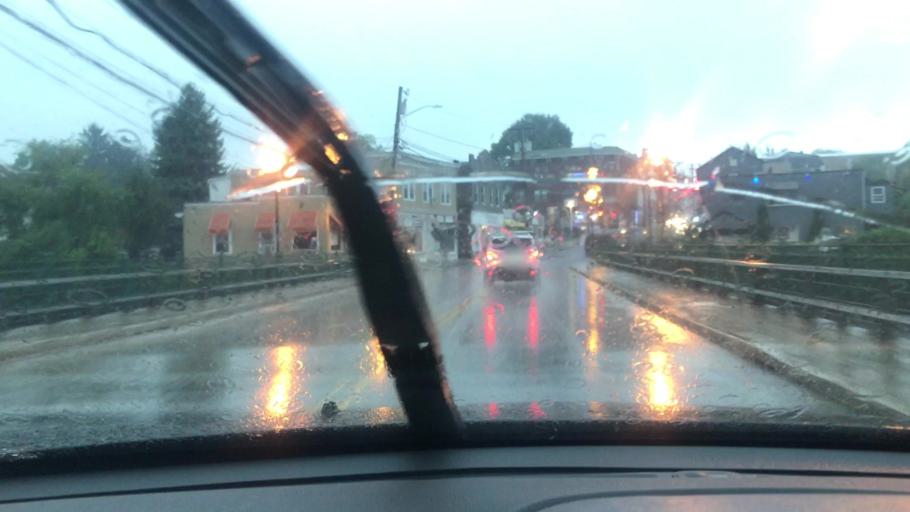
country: US
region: Connecticut
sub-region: Fairfield County
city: Byram
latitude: 41.0040
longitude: -73.6589
